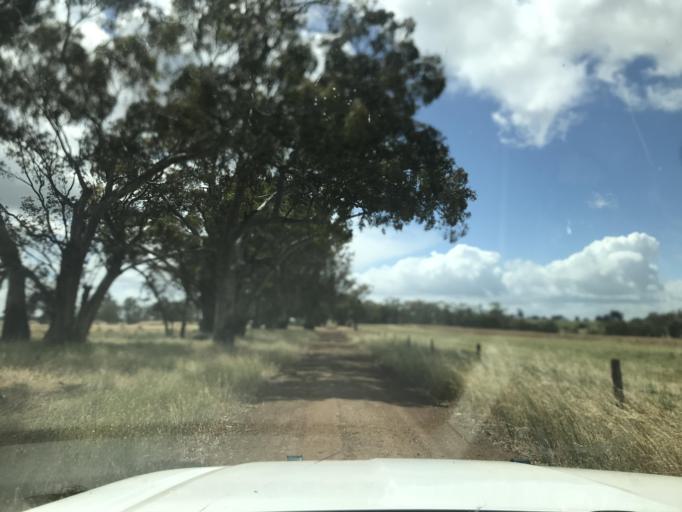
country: AU
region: South Australia
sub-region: Wattle Range
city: Penola
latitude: -37.1851
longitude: 141.4795
